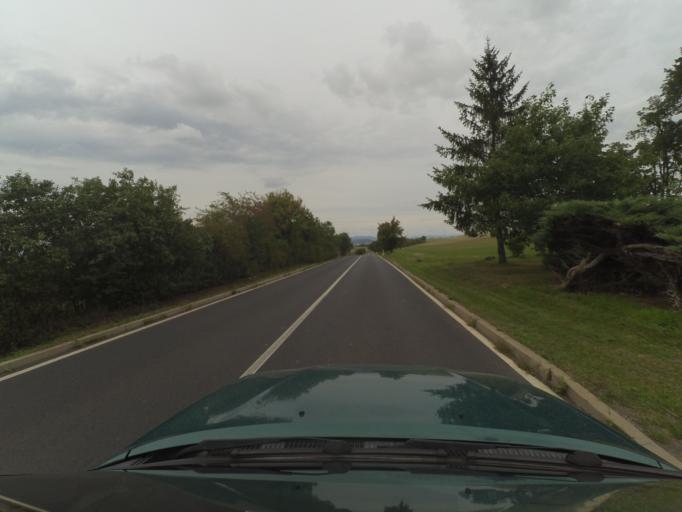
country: CZ
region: Ustecky
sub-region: Okres Louny
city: Louny
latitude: 50.3159
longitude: 13.8041
